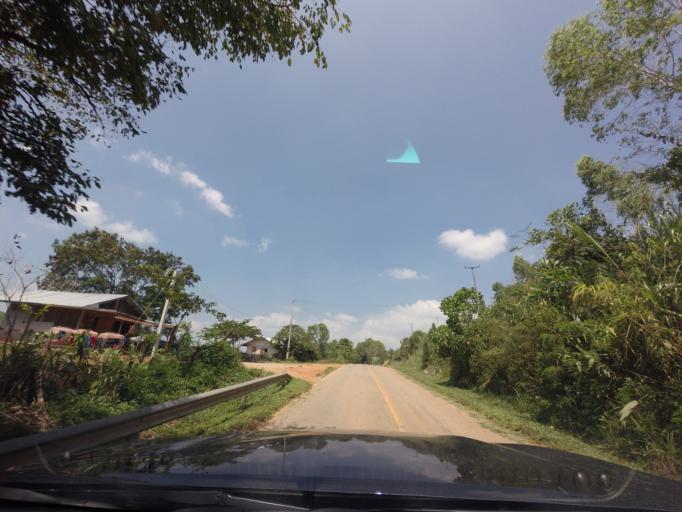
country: TH
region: Loei
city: Na Haeo
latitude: 17.5957
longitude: 100.9039
